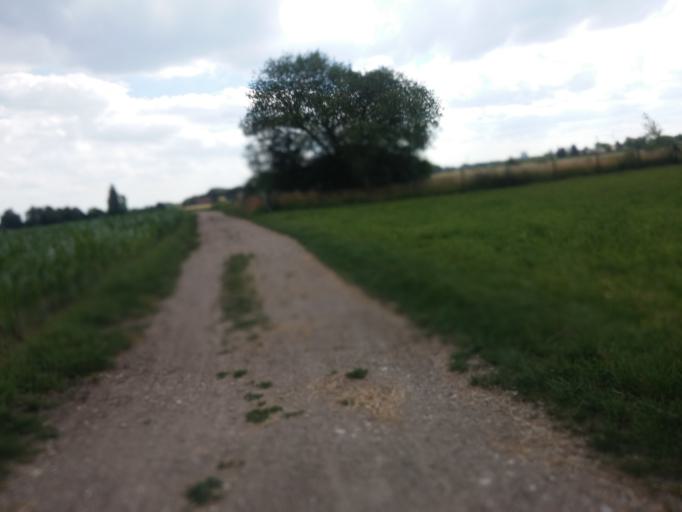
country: DE
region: Bavaria
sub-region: Upper Bavaria
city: Unterfoehring
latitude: 48.1592
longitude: 11.6648
